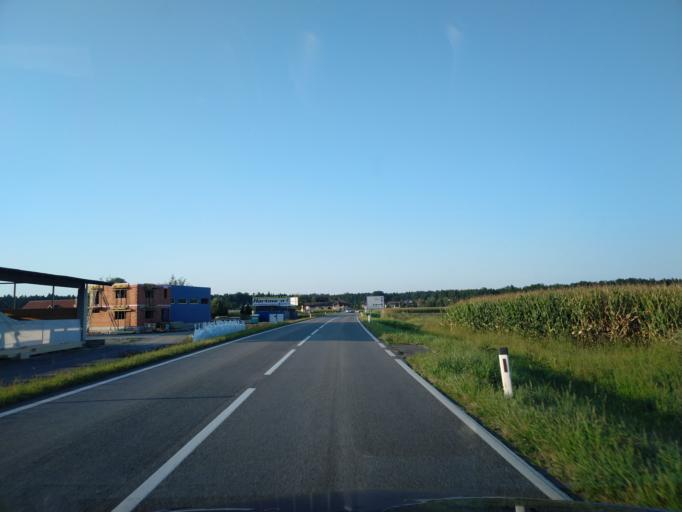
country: AT
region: Styria
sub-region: Politischer Bezirk Deutschlandsberg
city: Sankt Martin im Sulmtal
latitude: 46.7442
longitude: 15.3251
